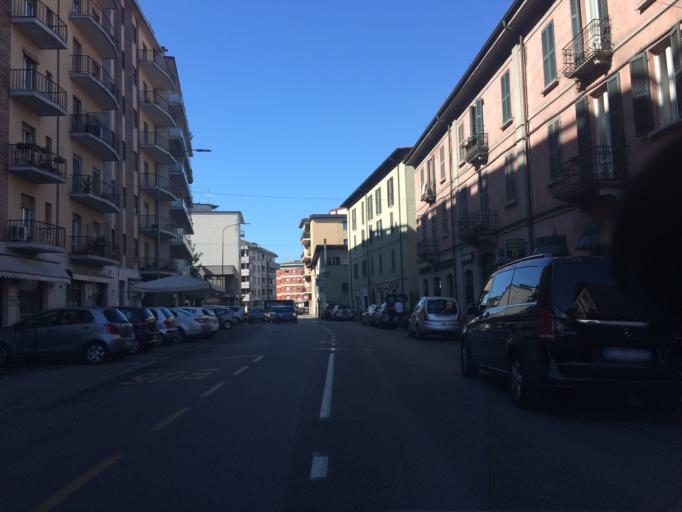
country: IT
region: Lombardy
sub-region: Provincia di Brescia
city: Brescia
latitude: 45.5293
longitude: 10.2066
